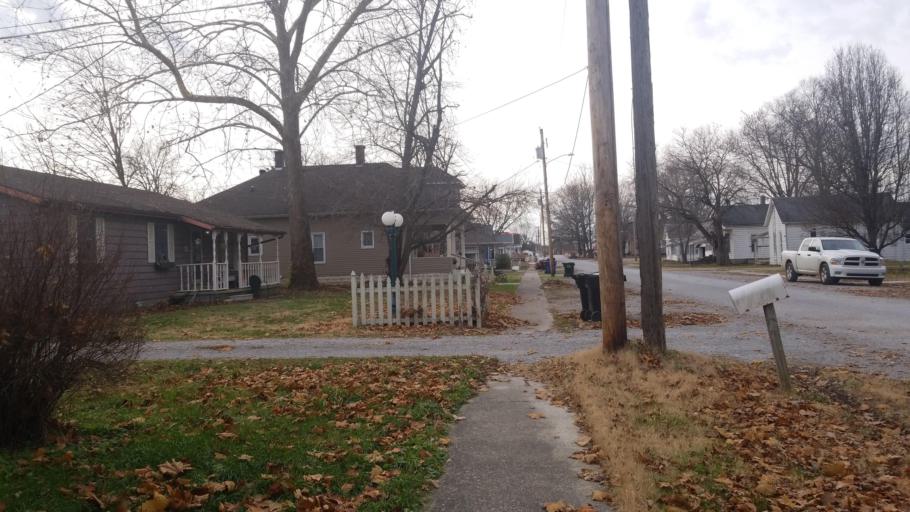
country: US
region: Illinois
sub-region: Saline County
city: Harrisburg
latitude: 37.8398
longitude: -88.6079
